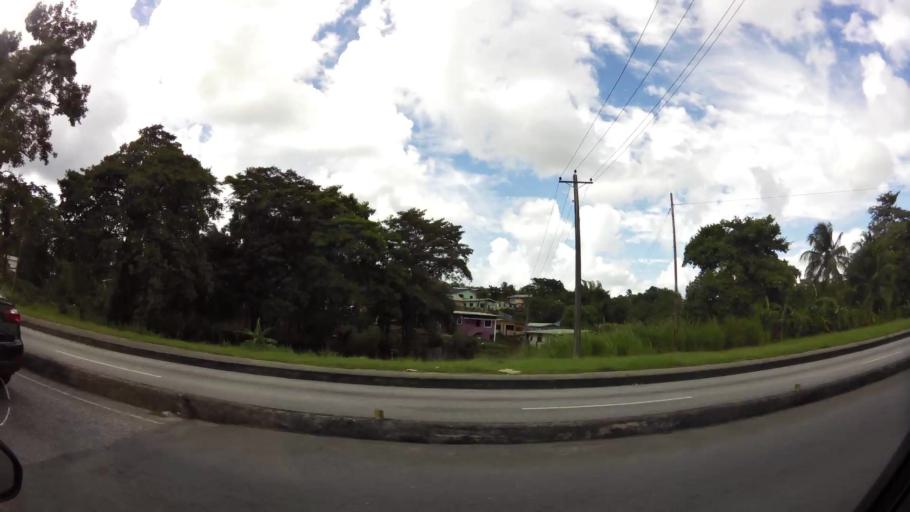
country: TT
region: City of San Fernando
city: Mon Repos
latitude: 10.2762
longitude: -61.4497
